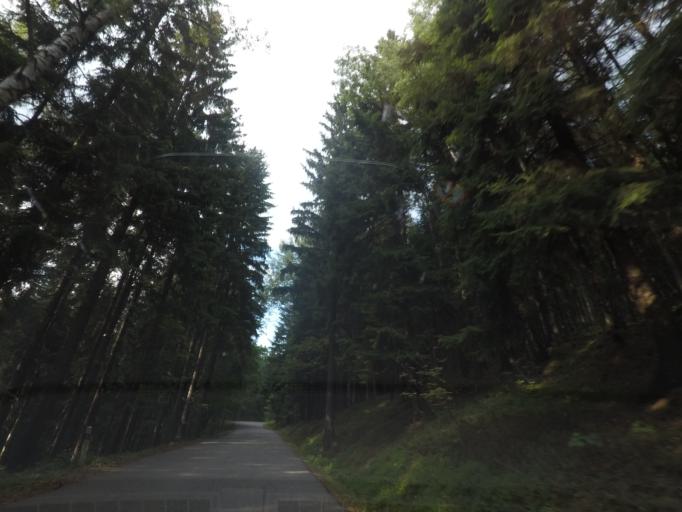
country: CZ
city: Radvanice
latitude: 50.6027
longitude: 16.0543
